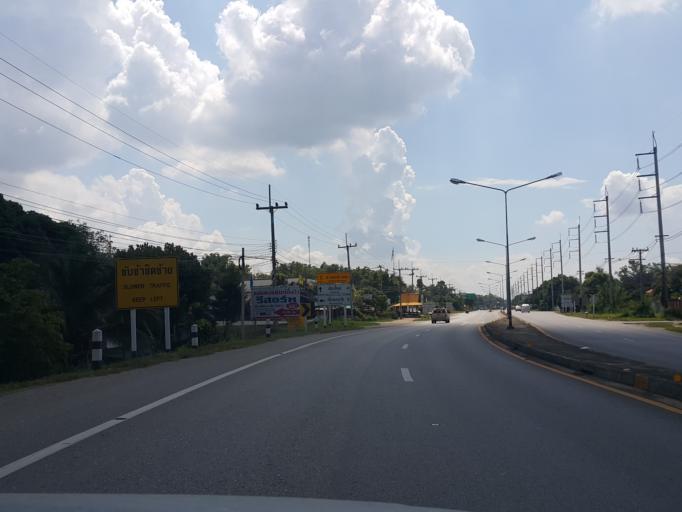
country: TH
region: Chiang Mai
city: Mae Taeng
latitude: 19.1381
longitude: 98.9481
